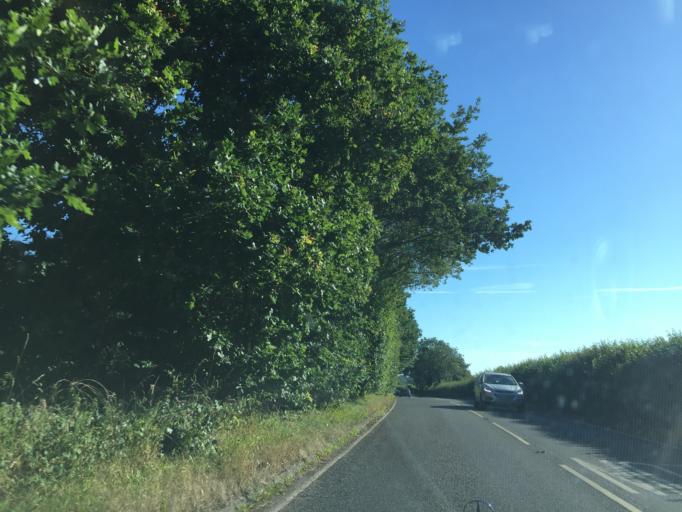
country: GB
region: England
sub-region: Warwickshire
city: Royal Leamington Spa
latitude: 52.3208
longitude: -1.5296
